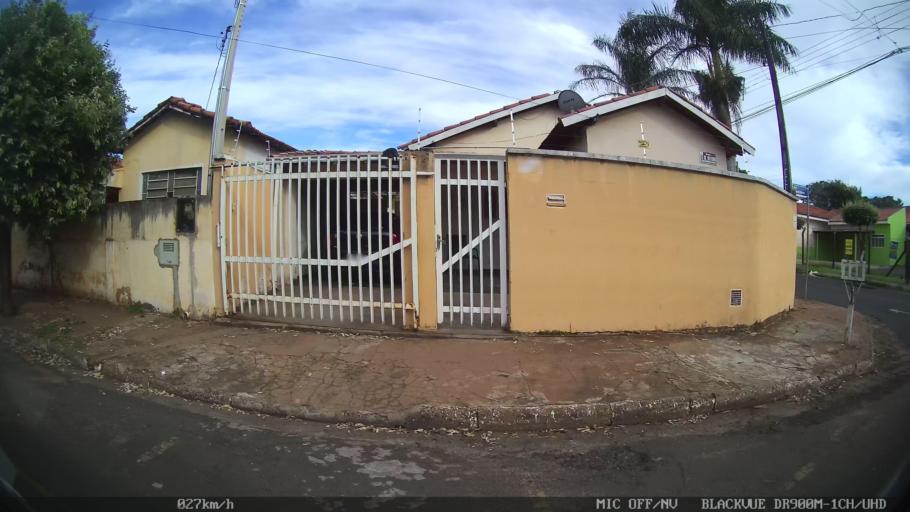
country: BR
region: Sao Paulo
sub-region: Catanduva
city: Catanduva
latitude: -21.1243
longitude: -48.9663
